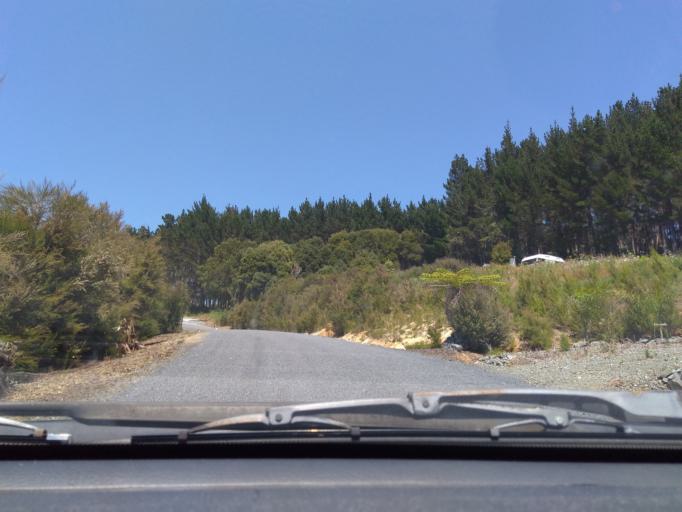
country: NZ
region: Northland
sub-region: Far North District
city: Taipa
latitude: -34.9974
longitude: 173.5115
